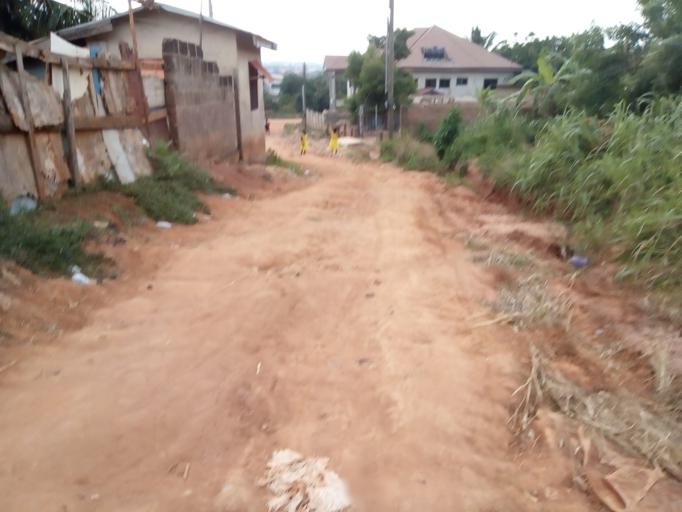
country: GH
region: Eastern
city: Nsawam
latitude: 5.7737
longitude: -0.3237
